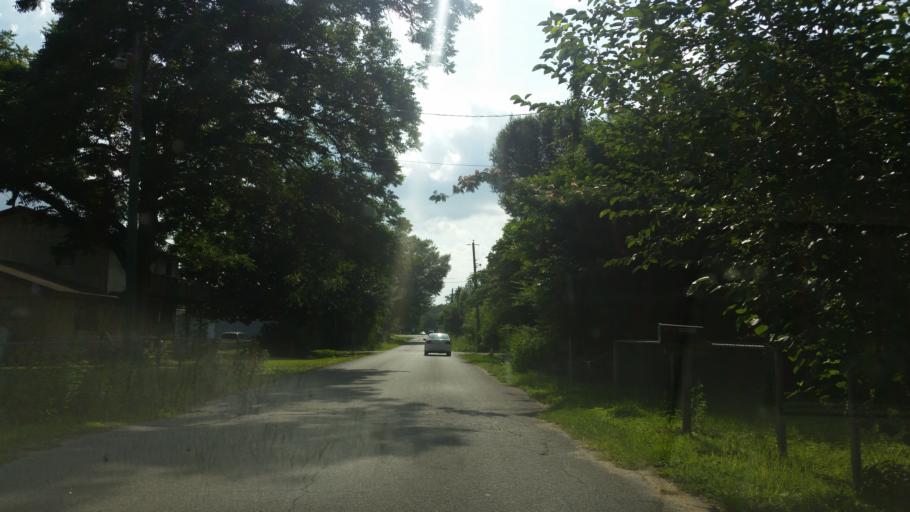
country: US
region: Florida
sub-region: Escambia County
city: Ensley
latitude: 30.5233
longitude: -87.2714
